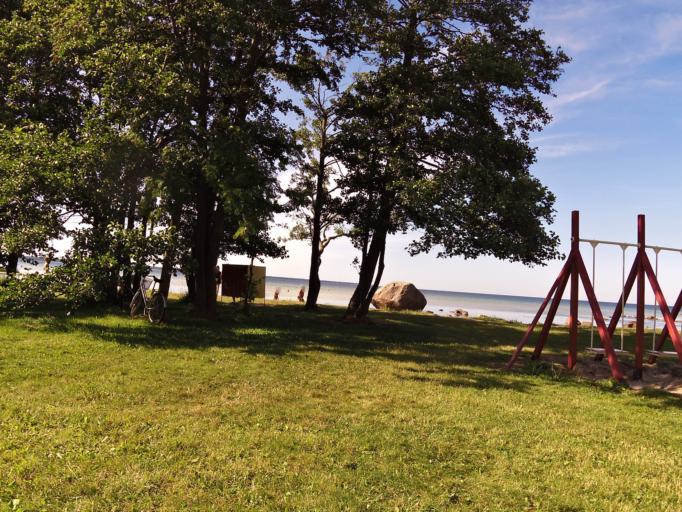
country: EE
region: Hiiumaa
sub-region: Kaerdla linn
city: Kardla
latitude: 59.0067
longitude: 22.7451
